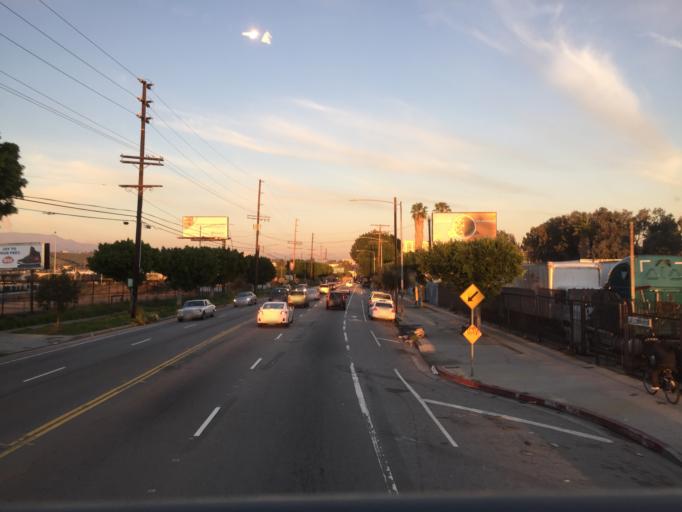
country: US
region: California
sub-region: Los Angeles County
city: Los Angeles
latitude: 34.0559
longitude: -118.2221
